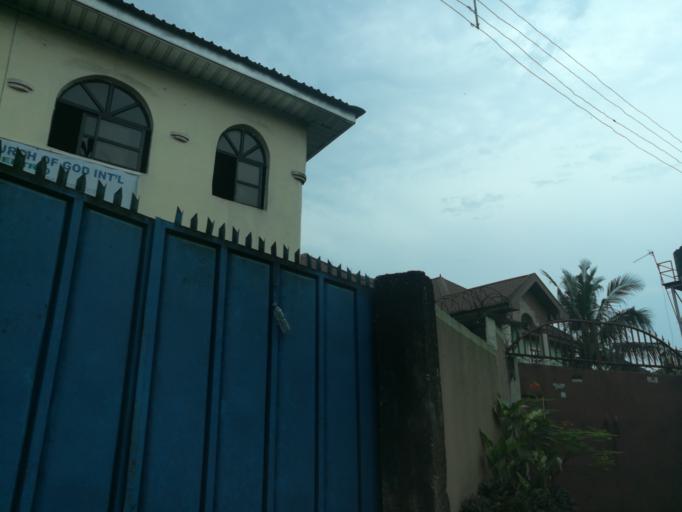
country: NG
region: Rivers
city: Port Harcourt
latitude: 4.8129
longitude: 7.0253
